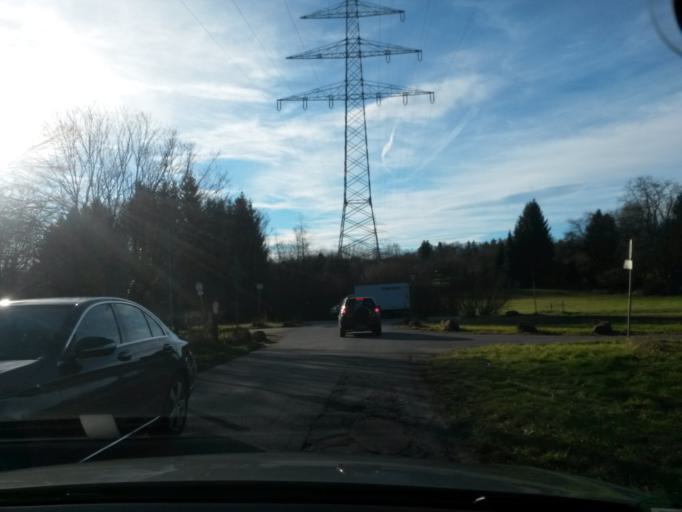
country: DE
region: Baden-Wuerttemberg
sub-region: Karlsruhe Region
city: Ispringen
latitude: 48.8974
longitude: 8.6458
